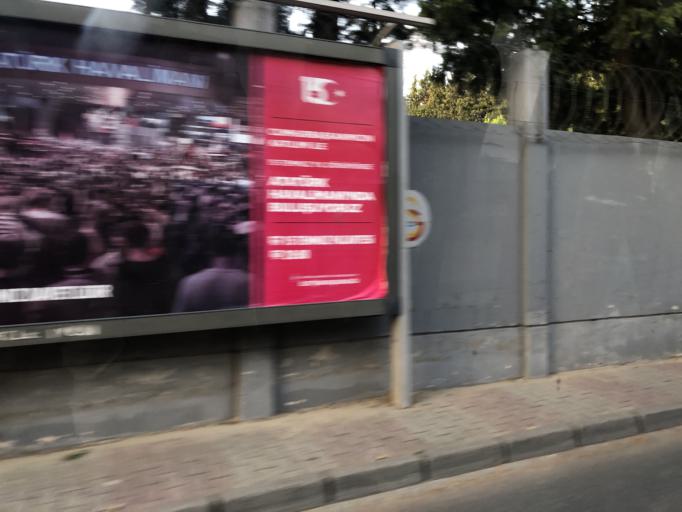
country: TR
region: Istanbul
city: Bahcelievler
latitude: 40.9738
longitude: 28.7979
